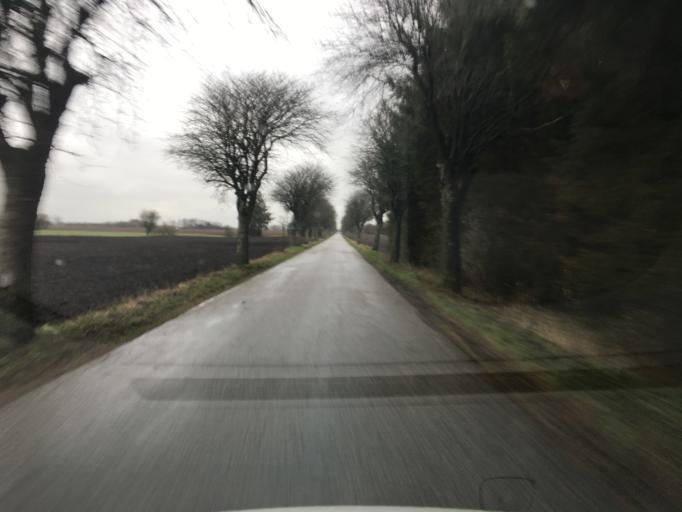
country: DK
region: South Denmark
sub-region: Aabenraa Kommune
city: Krusa
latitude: 54.9005
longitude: 9.3577
